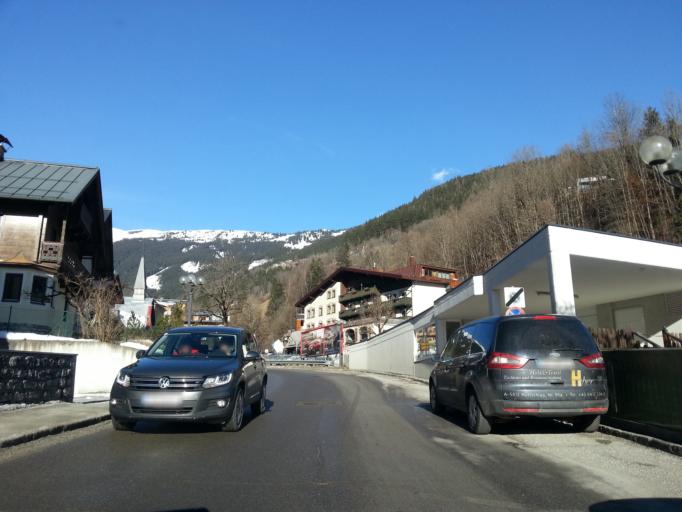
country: AT
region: Salzburg
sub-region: Politischer Bezirk Zell am See
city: Zell am See
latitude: 47.3243
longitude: 12.7924
